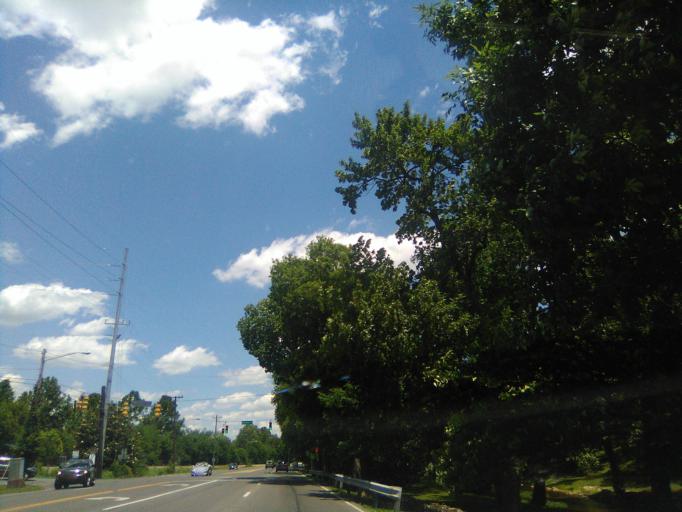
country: US
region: Tennessee
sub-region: Davidson County
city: Belle Meade
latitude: 36.1145
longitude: -86.8616
